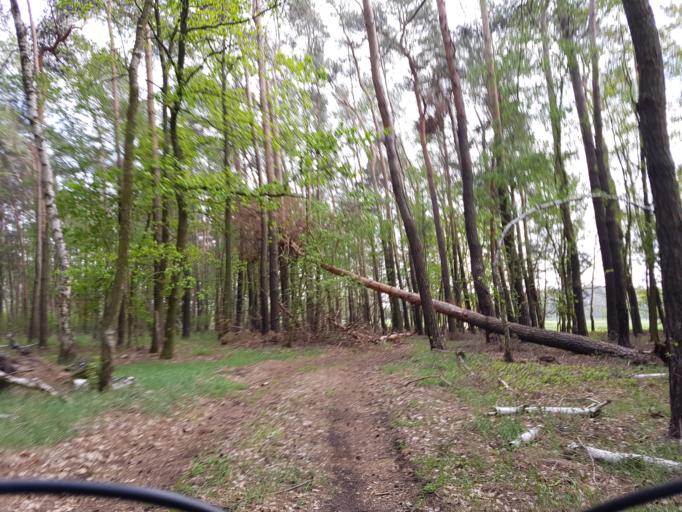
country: DE
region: Brandenburg
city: Schilda
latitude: 51.5947
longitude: 13.3708
